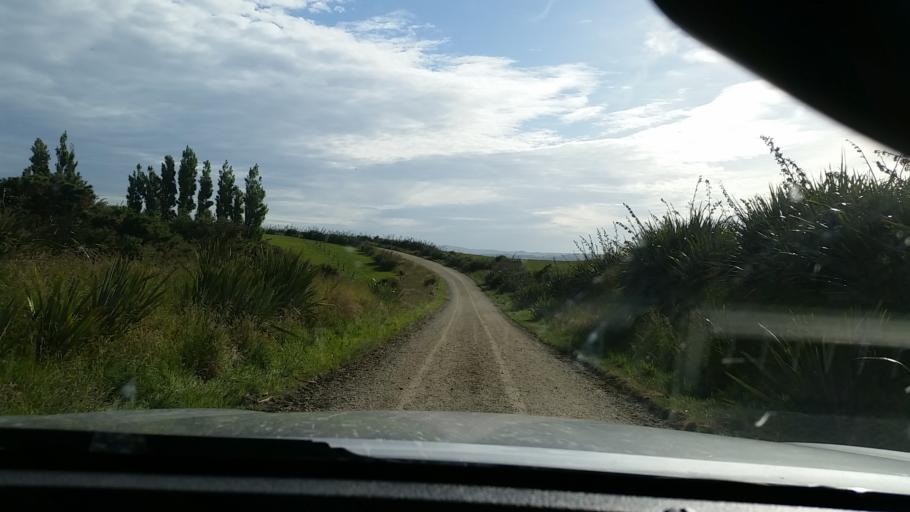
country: NZ
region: Southland
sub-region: Gore District
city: Gore
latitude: -46.2347
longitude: 168.7680
